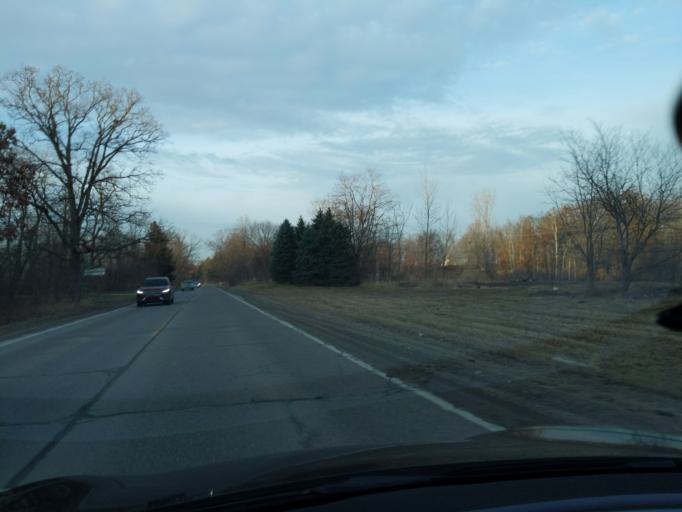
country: US
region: Michigan
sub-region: Livingston County
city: Brighton
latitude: 42.6084
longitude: -83.7481
